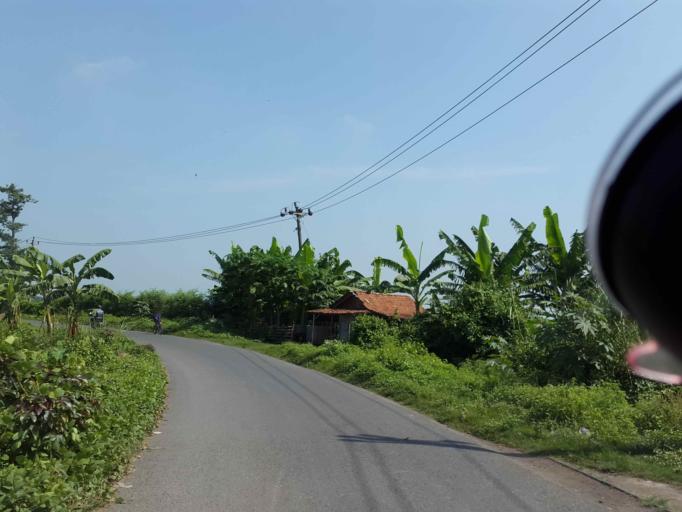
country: ID
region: Central Java
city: Pemalang
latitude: -6.9249
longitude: 109.3378
